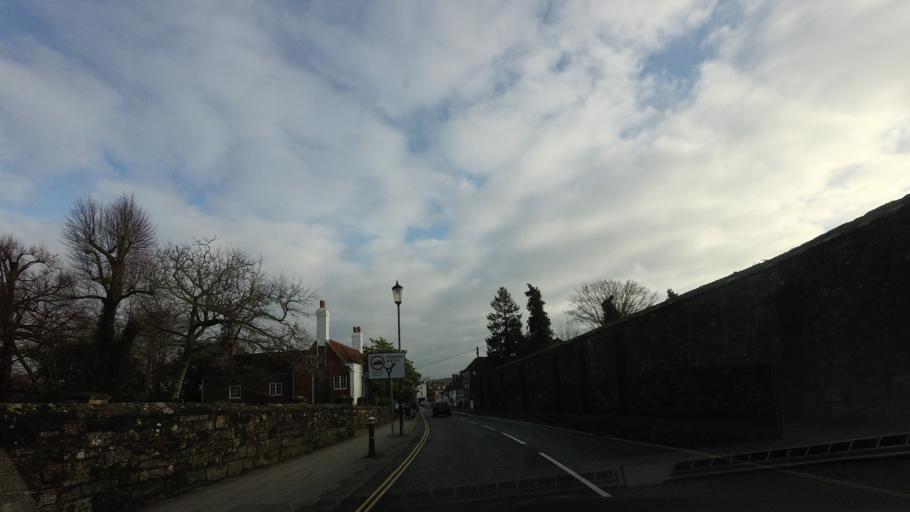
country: GB
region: England
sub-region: East Sussex
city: Battle
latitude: 50.9147
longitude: 0.4886
